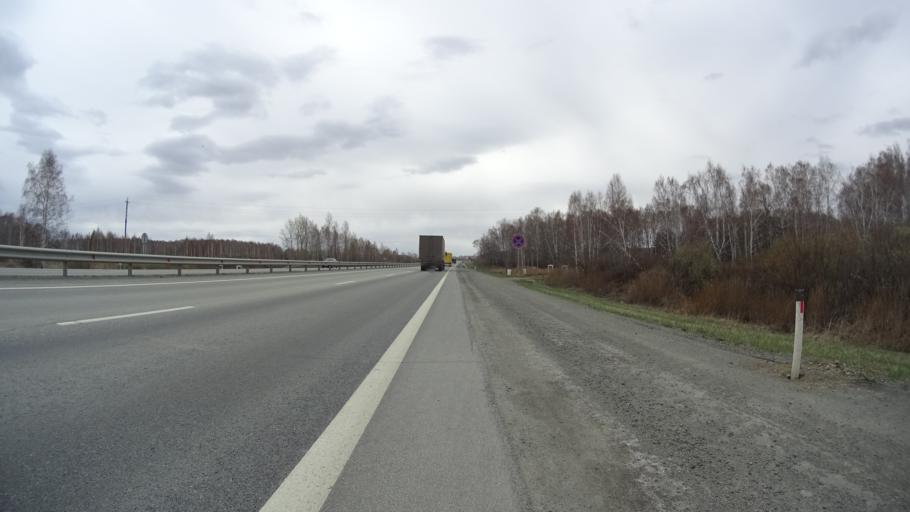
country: RU
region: Chelyabinsk
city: Yemanzhelinka
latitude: 54.8285
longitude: 61.3109
